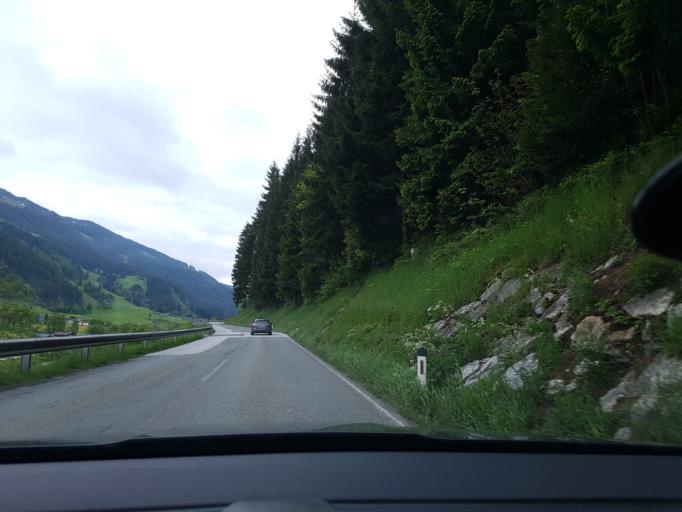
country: AT
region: Tyrol
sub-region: Politischer Bezirk Kitzbuhel
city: Jochberg
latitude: 47.3685
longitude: 12.4162
